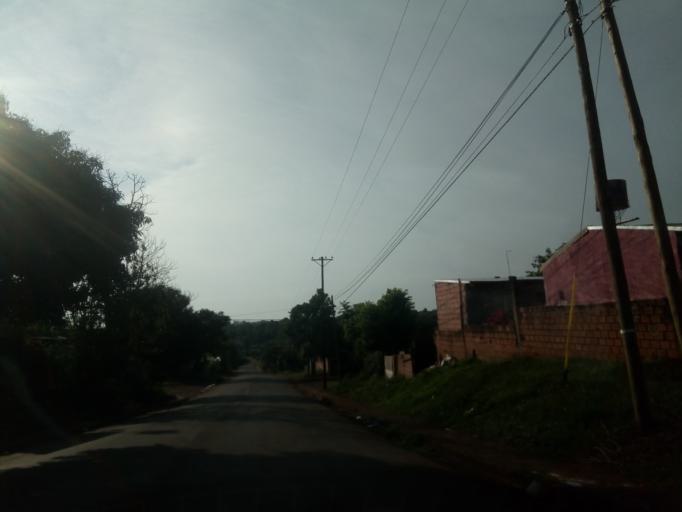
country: AR
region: Misiones
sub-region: Departamento de Capital
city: Posadas
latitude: -27.4302
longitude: -55.9118
